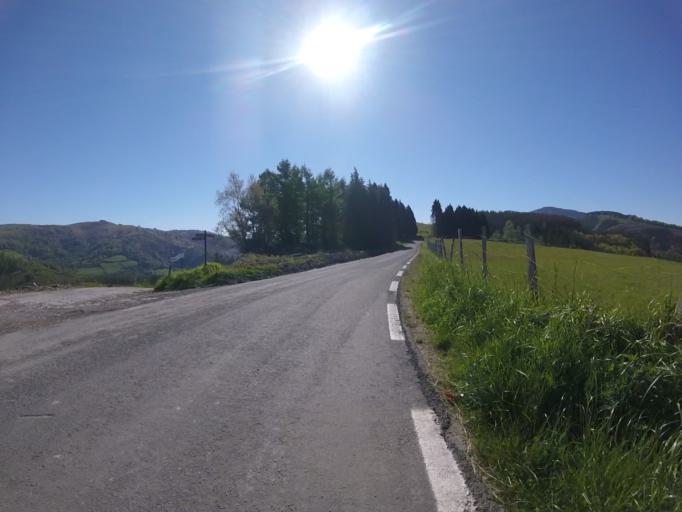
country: ES
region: Basque Country
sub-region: Provincia de Guipuzcoa
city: Aizarnazabal
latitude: 43.2141
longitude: -2.2047
